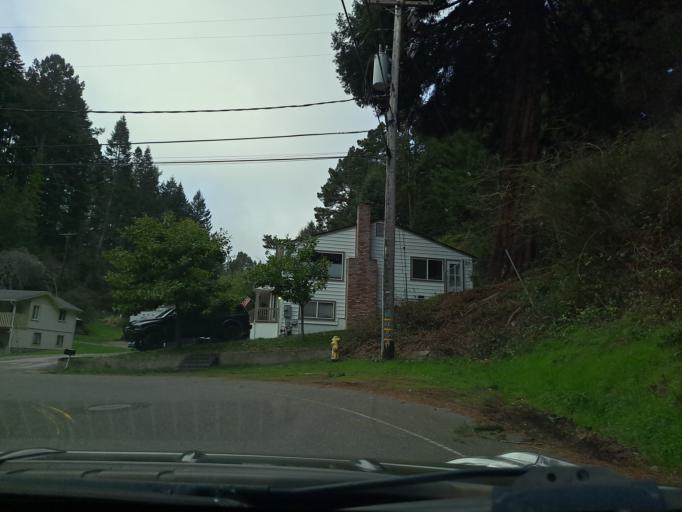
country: US
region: California
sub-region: Humboldt County
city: Fortuna
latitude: 40.6038
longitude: -124.1609
